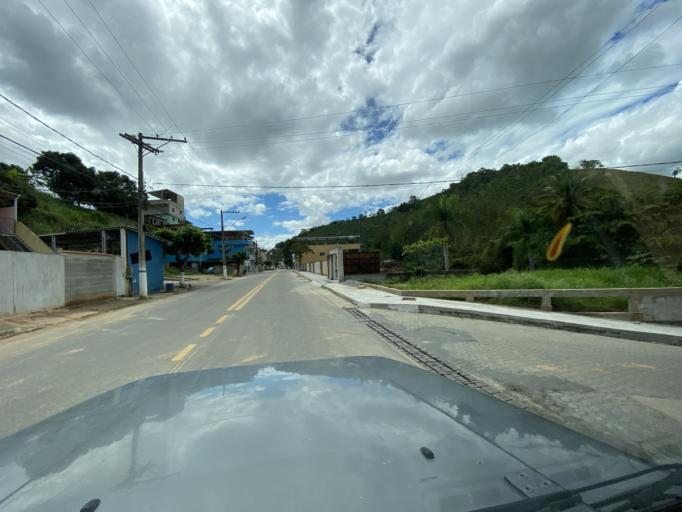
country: BR
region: Espirito Santo
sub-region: Jeronimo Monteiro
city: Jeronimo Monteiro
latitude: -20.7922
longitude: -41.3802
